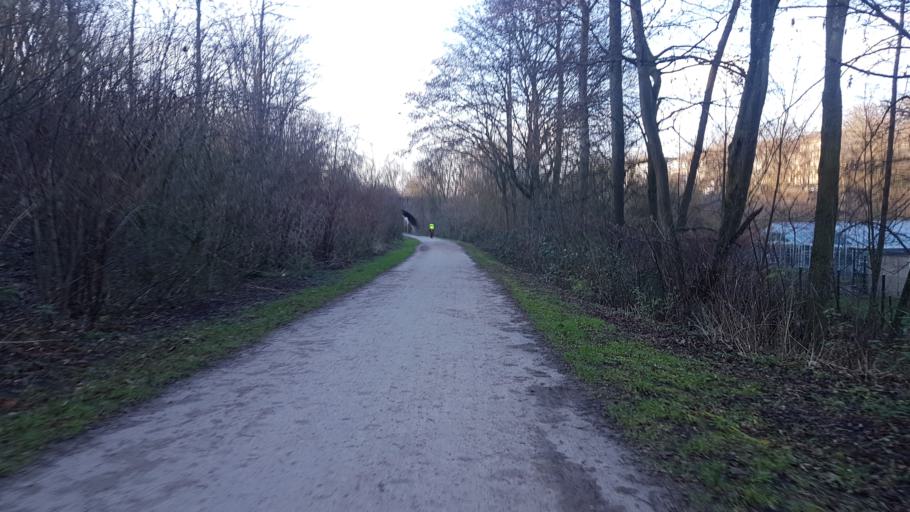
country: DE
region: North Rhine-Westphalia
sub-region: Regierungsbezirk Dusseldorf
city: Essen
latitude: 51.4343
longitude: 6.9816
